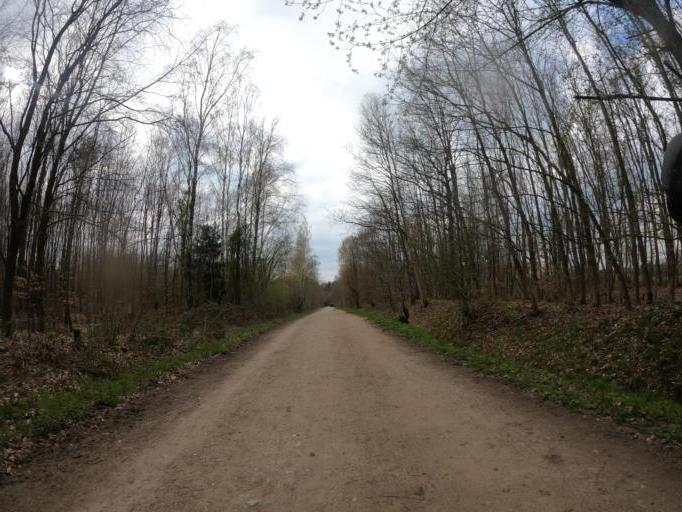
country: DE
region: North Rhine-Westphalia
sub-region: Regierungsbezirk Koln
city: Aachen
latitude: 50.7414
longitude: 6.1226
